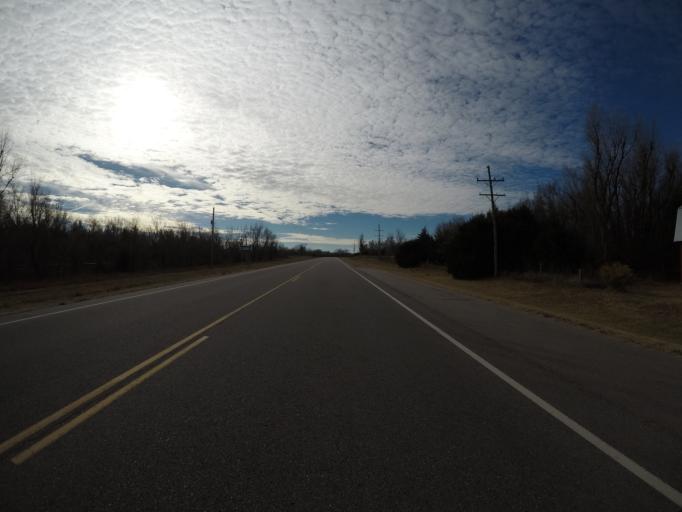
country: US
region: Kansas
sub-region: Reno County
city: Hutchinson
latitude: 38.1146
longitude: -97.8647
